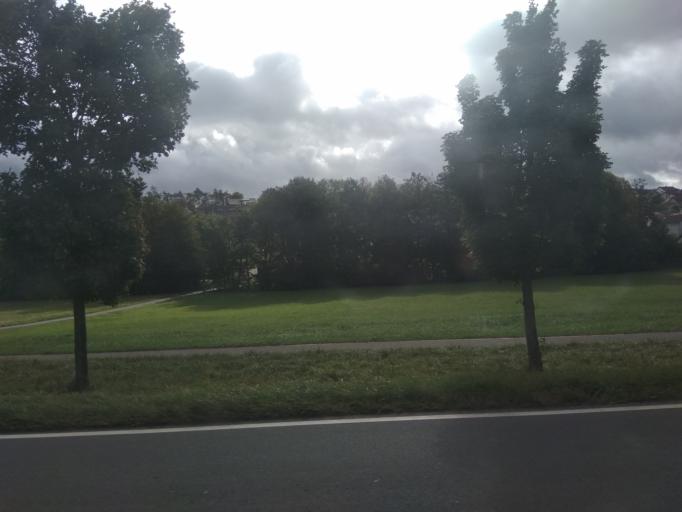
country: DE
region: Baden-Wuerttemberg
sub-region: Karlsruhe Region
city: Billigheim
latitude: 49.4071
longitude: 9.2783
